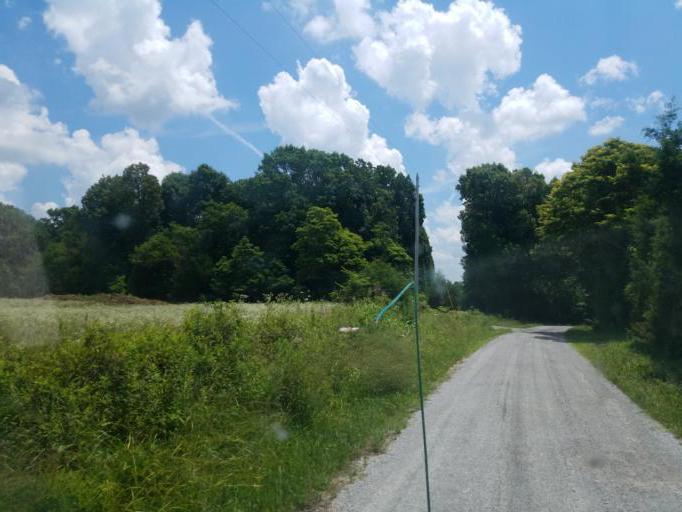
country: US
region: Kentucky
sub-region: Grayson County
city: Leitchfield
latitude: 37.4799
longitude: -86.4601
